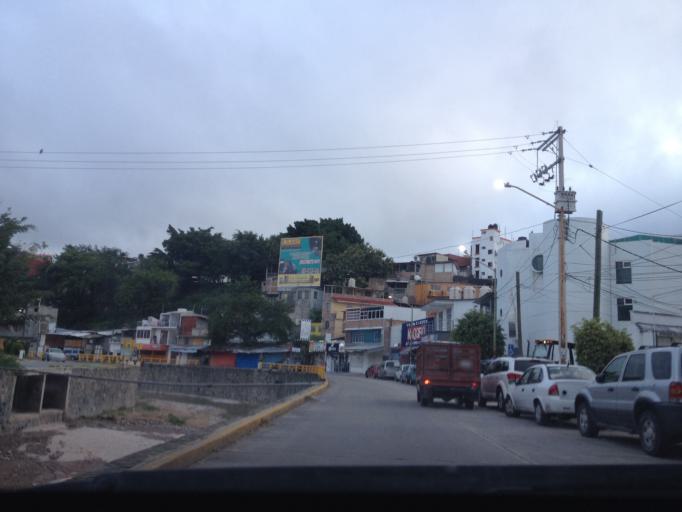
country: MX
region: Guerrero
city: Chilpancingo de los Bravos
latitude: 17.5480
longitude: -99.5022
